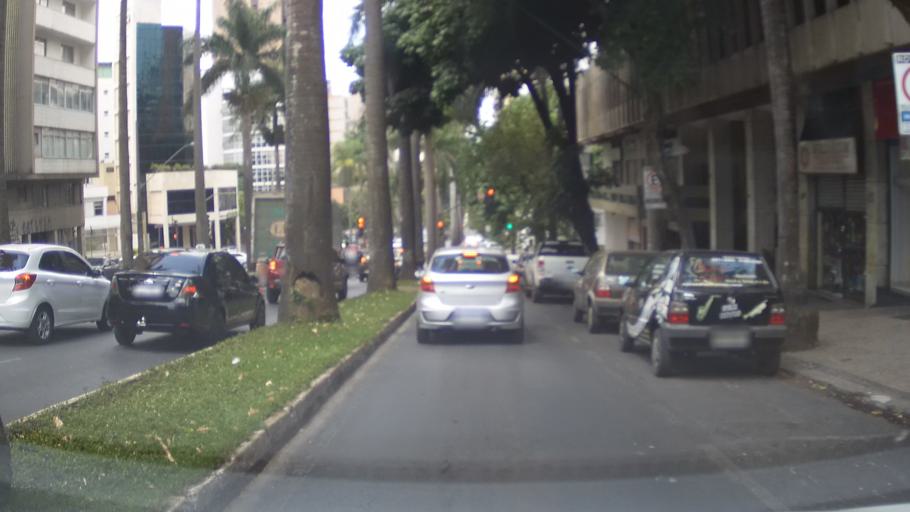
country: BR
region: Minas Gerais
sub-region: Belo Horizonte
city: Belo Horizonte
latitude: -19.9322
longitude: -43.9359
